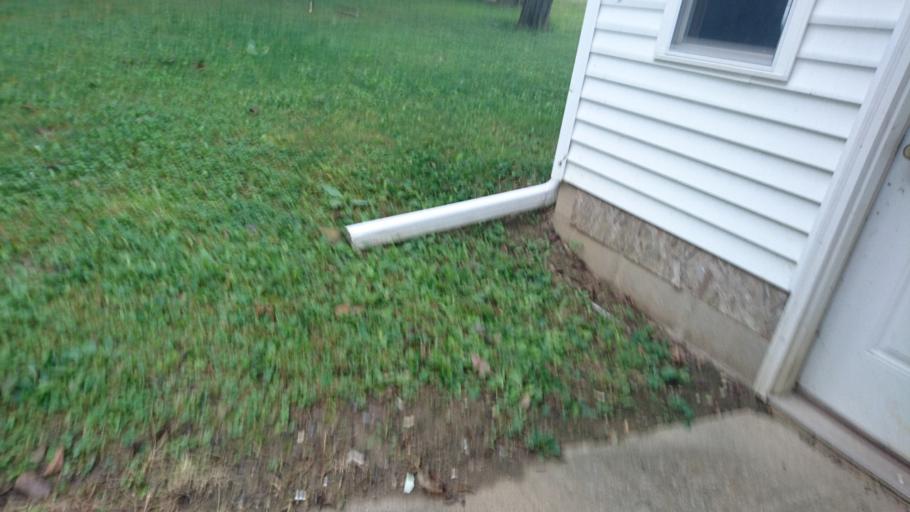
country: US
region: Illinois
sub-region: Logan County
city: Atlanta
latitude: 40.2263
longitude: -89.1974
